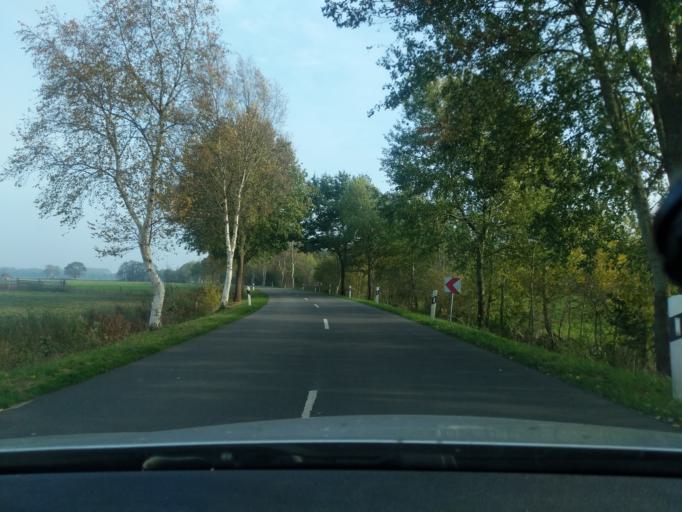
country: DE
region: Lower Saxony
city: Stinstedt
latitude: 53.6489
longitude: 8.9924
